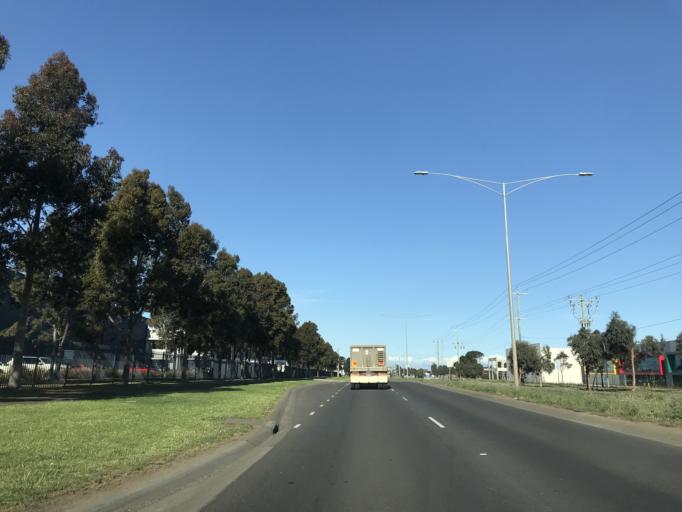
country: AU
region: Victoria
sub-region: Wyndham
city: Truganina
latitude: -37.8114
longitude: 144.7623
